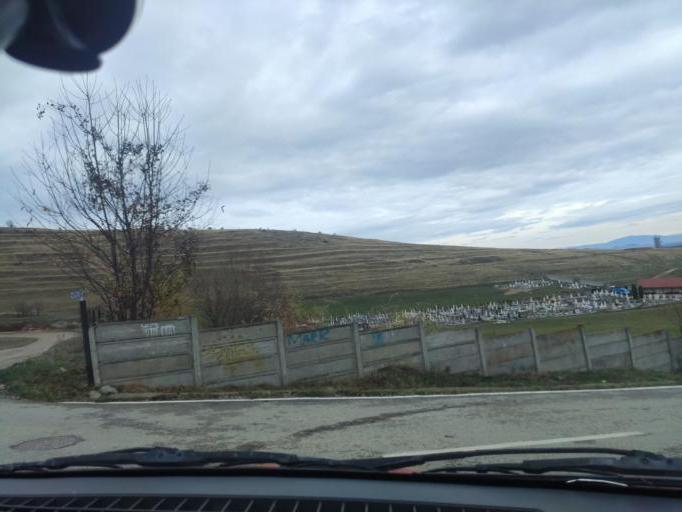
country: RO
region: Brasov
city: Codlea
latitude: 45.7080
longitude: 25.4434
